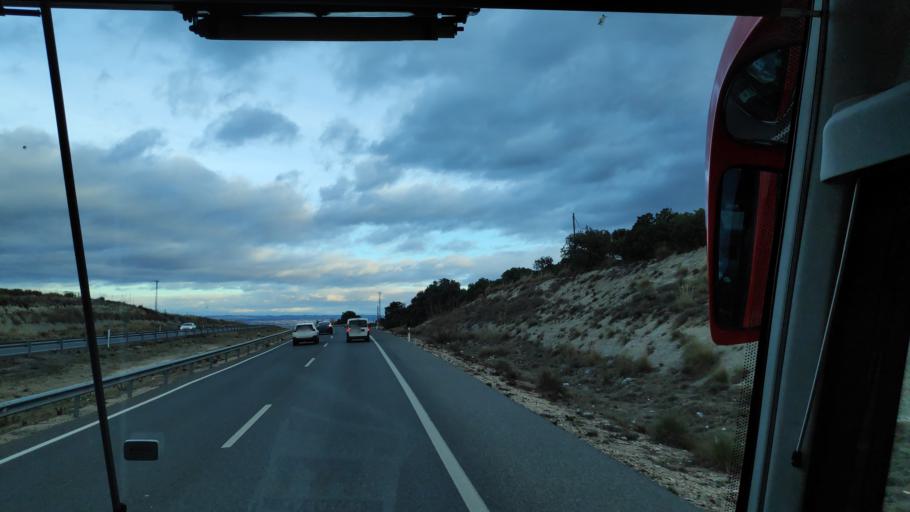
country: ES
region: Madrid
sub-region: Provincia de Madrid
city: Fuentiduena de Tajo
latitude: 40.1406
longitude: -3.2026
